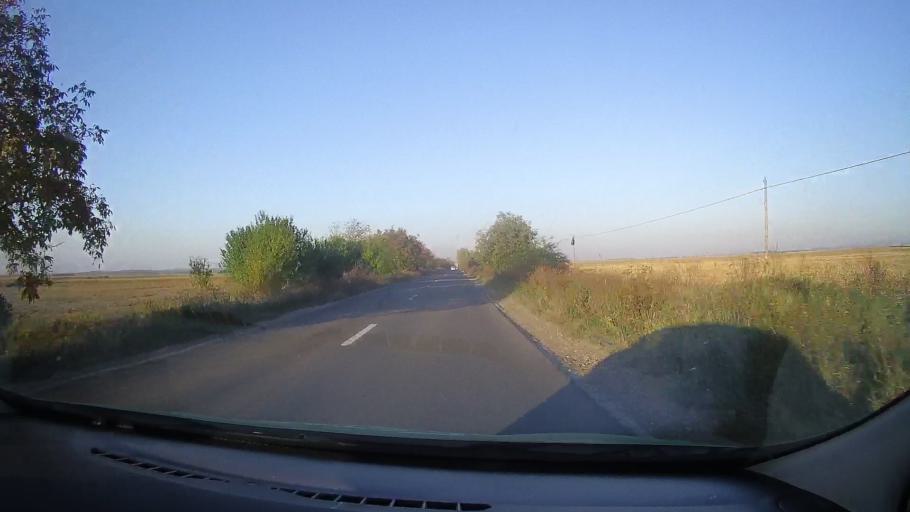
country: RO
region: Bihor
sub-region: Comuna Salard
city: Salard
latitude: 47.1908
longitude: 21.9948
